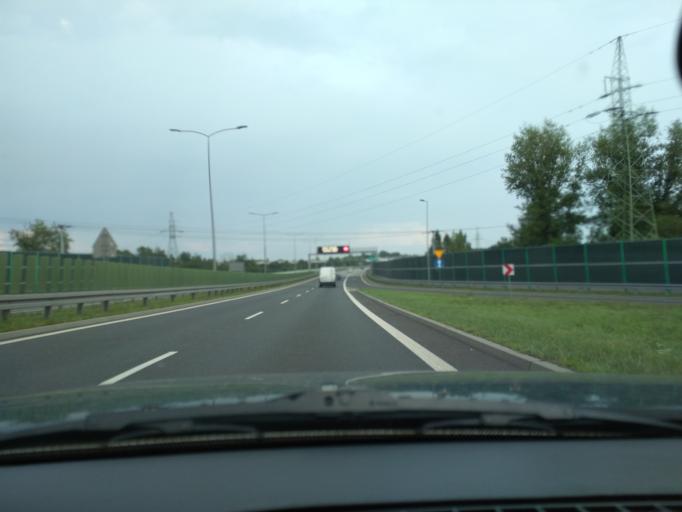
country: PL
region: Silesian Voivodeship
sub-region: Gliwice
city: Gliwice
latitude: 50.2884
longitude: 18.7029
